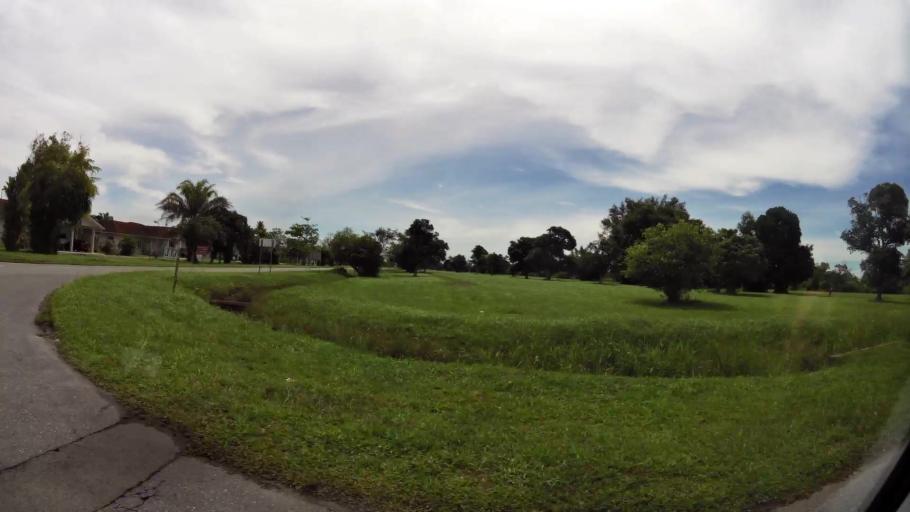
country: BN
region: Belait
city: Seria
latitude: 4.6033
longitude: 114.3176
